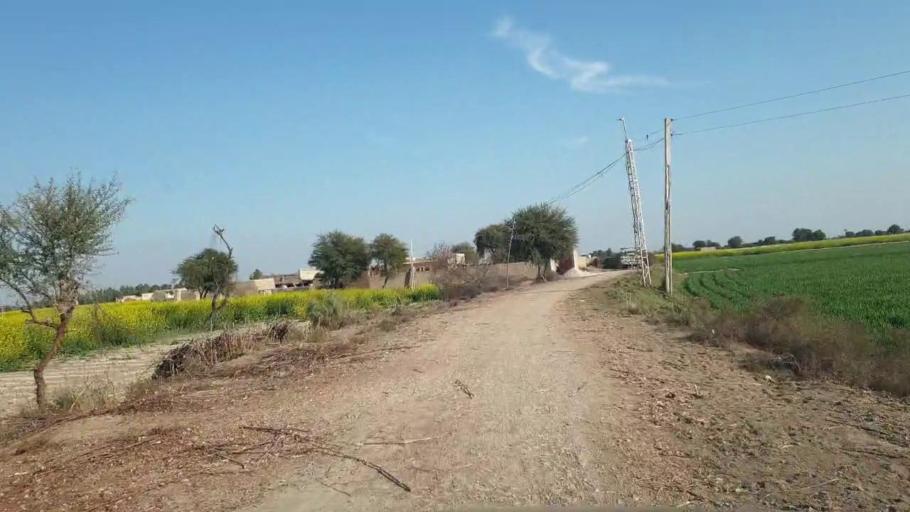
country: PK
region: Sindh
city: Shahpur Chakar
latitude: 26.1755
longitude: 68.6698
